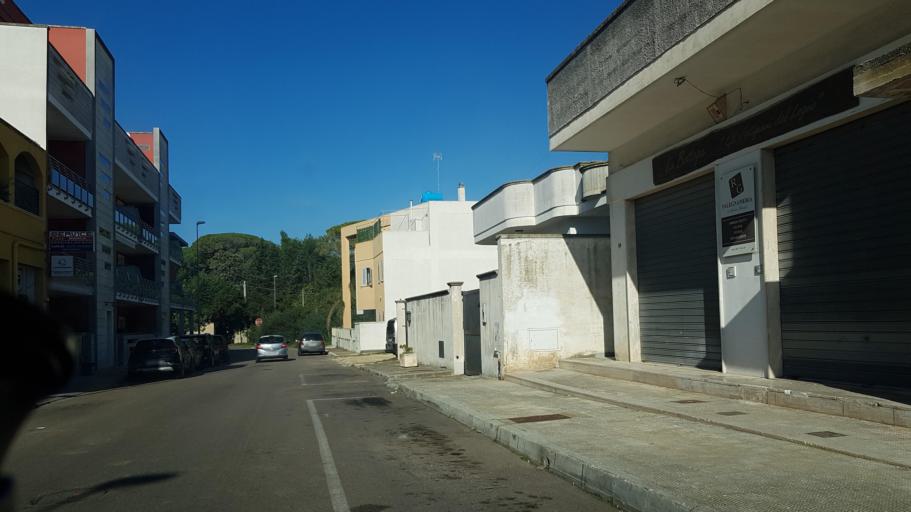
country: IT
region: Apulia
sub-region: Provincia di Lecce
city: Arnesano
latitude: 40.3312
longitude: 18.1007
